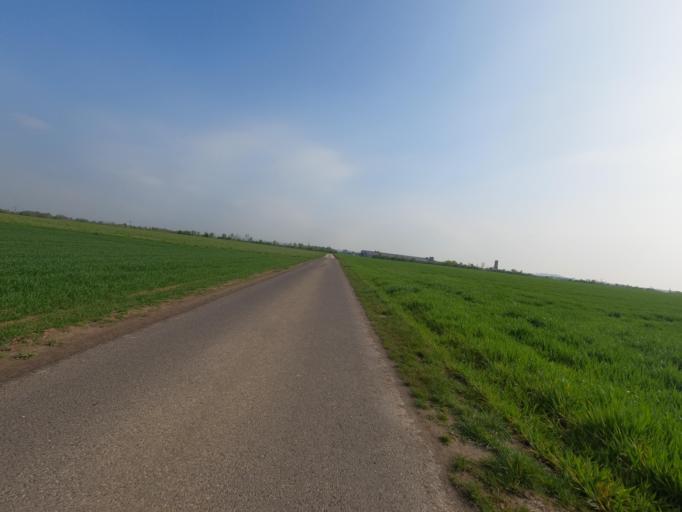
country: DE
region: North Rhine-Westphalia
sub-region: Regierungsbezirk Koln
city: Heinsberg
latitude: 51.0377
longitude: 6.1146
